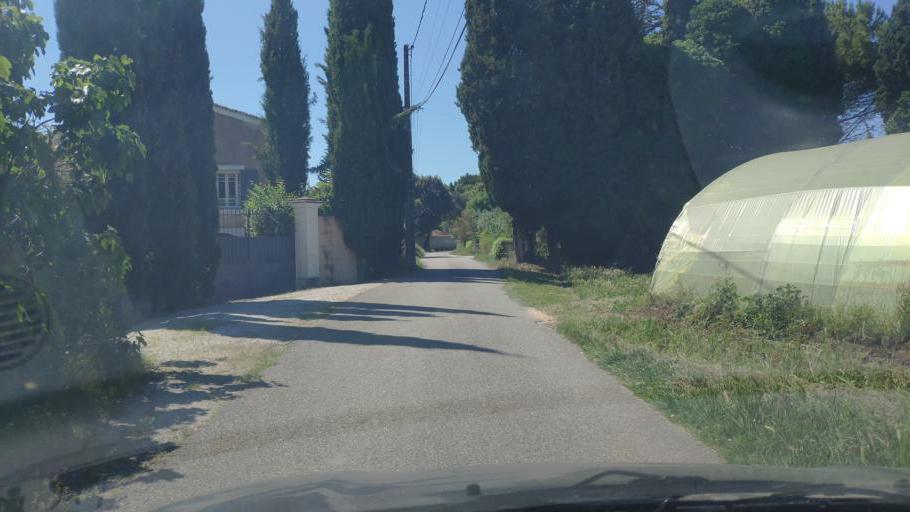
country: FR
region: Provence-Alpes-Cote d'Azur
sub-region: Departement du Vaucluse
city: Loriol-du-Comtat
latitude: 44.0696
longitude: 5.0253
